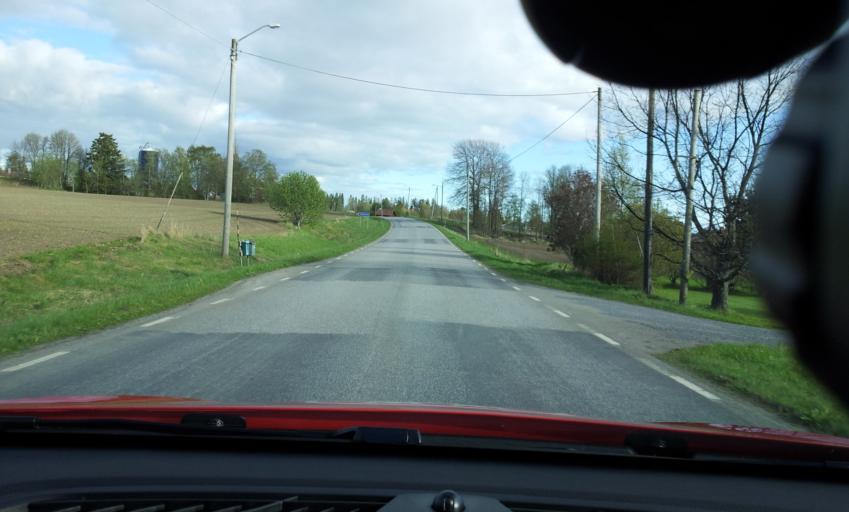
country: SE
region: Jaemtland
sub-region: Krokoms Kommun
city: Krokom
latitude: 63.2557
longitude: 14.4088
